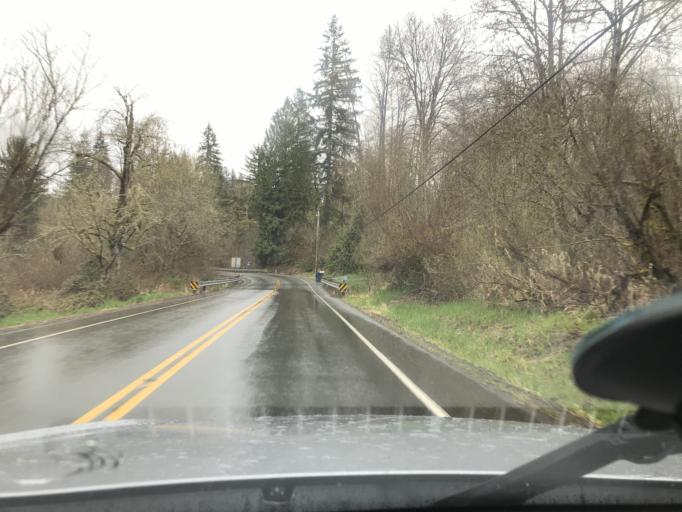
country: US
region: Washington
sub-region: King County
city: Ames Lake
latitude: 47.6623
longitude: -121.9694
